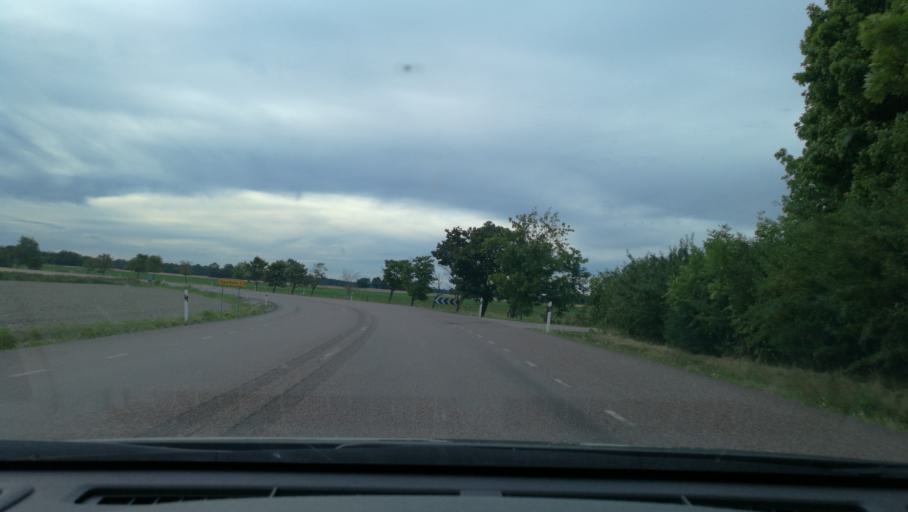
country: SE
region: Vaestmanland
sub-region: Kungsors Kommun
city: Kungsoer
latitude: 59.4326
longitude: 16.0839
